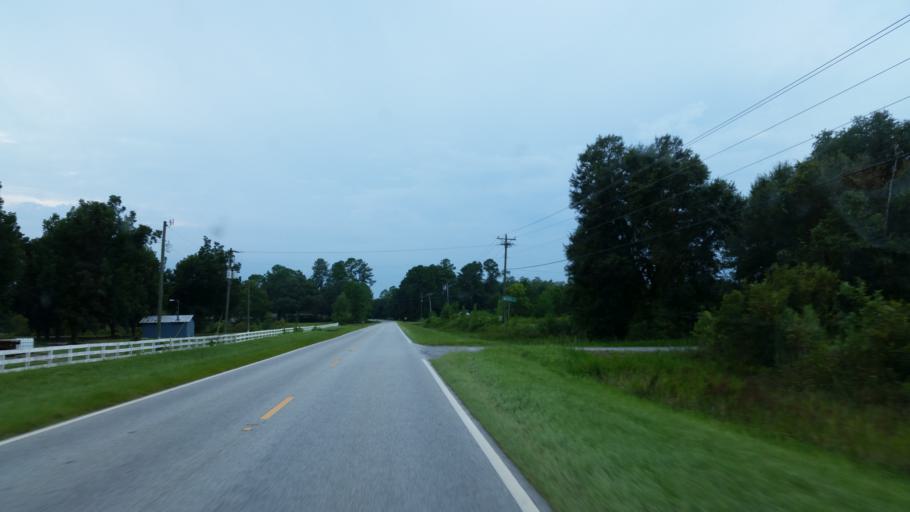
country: US
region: Georgia
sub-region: Lowndes County
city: Valdosta
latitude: 30.7385
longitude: -83.3144
